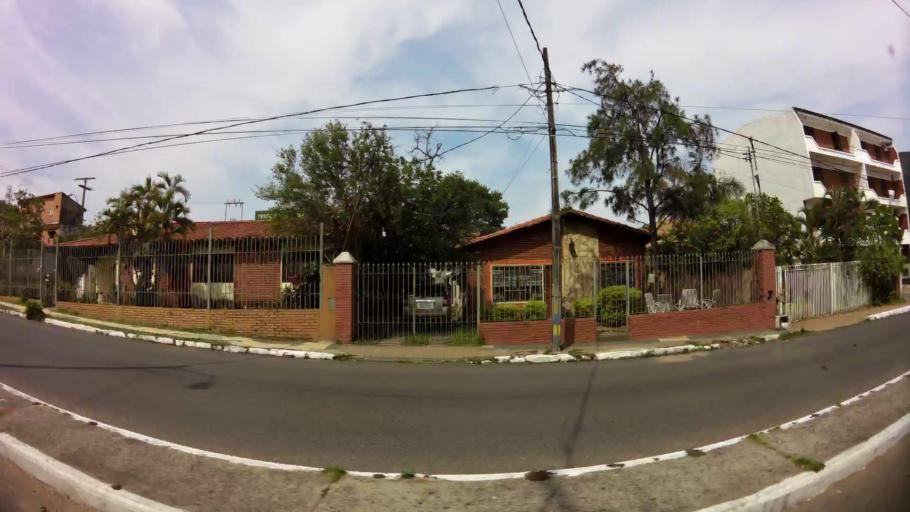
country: PY
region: Asuncion
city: Asuncion
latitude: -25.2568
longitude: -57.5832
